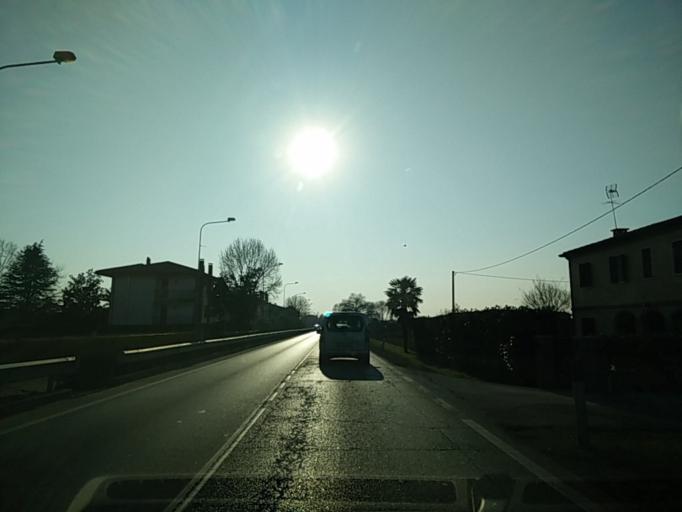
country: IT
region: Veneto
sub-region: Provincia di Venezia
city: San Dona di Piave
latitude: 45.6524
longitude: 12.6039
